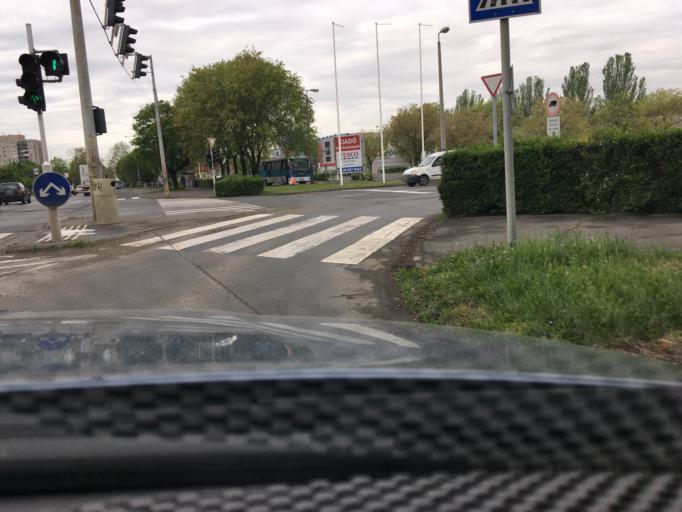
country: HU
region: Hajdu-Bihar
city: Debrecen
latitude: 47.5295
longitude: 21.6092
